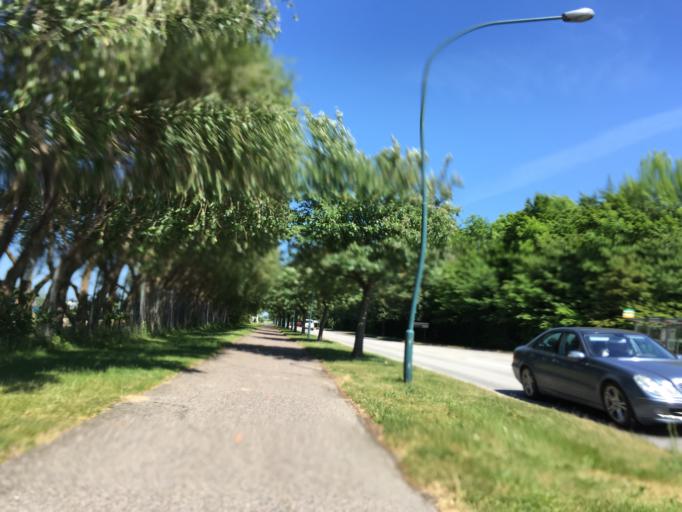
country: SE
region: Skane
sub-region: Trelleborgs Kommun
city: Trelleborg
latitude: 55.3775
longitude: 13.1231
